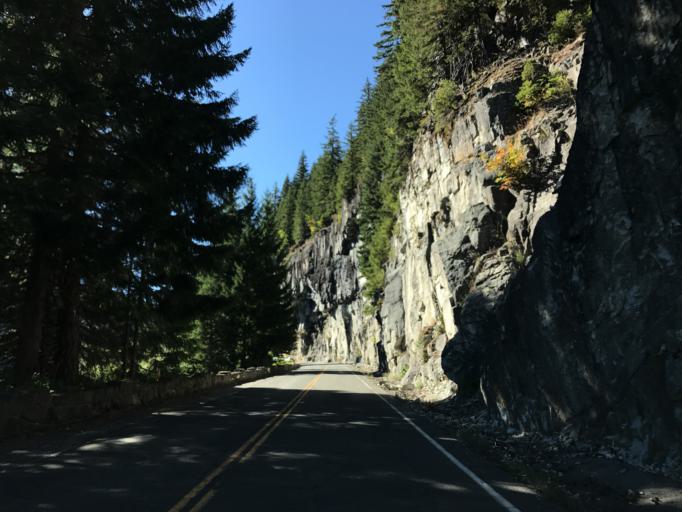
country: US
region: Washington
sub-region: Pierce County
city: Buckley
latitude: 46.7624
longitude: -121.6586
